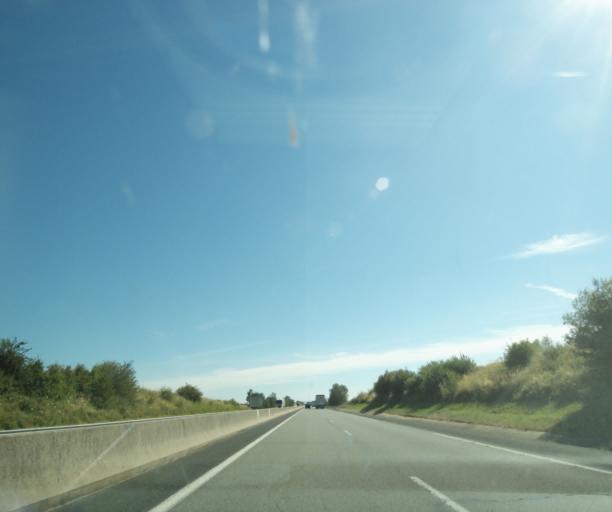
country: FR
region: Lorraine
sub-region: Departement des Vosges
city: Lamarche
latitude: 48.1643
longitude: 5.7080
